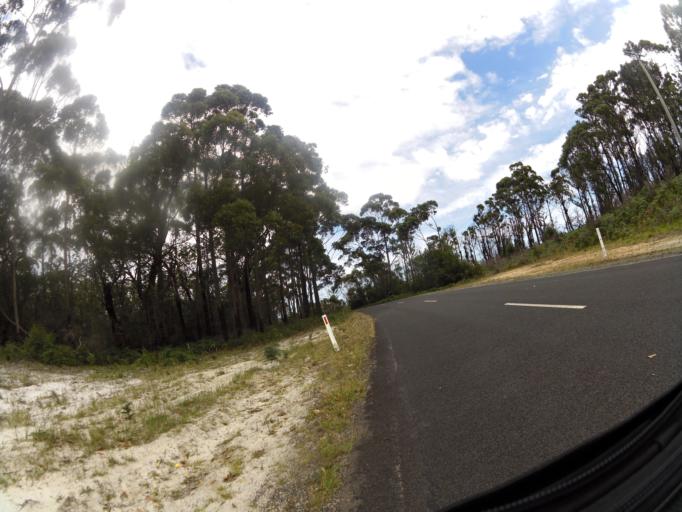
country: AU
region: Victoria
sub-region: East Gippsland
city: Lakes Entrance
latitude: -37.7828
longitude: 148.7300
